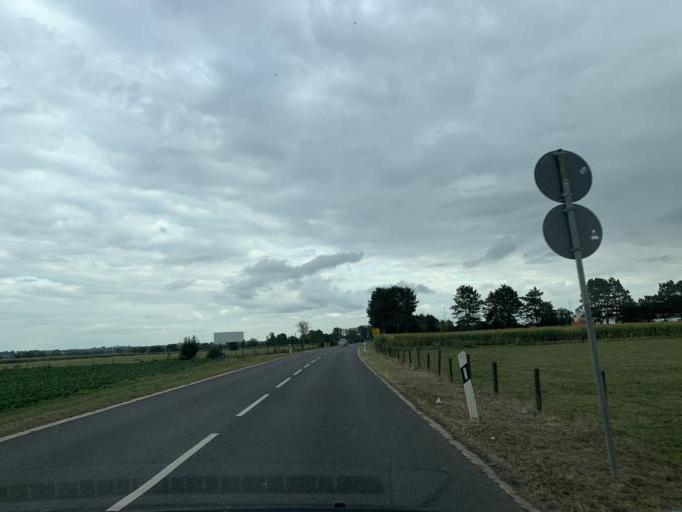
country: DE
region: North Rhine-Westphalia
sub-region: Regierungsbezirk Koln
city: Linnich
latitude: 51.0113
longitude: 6.2404
